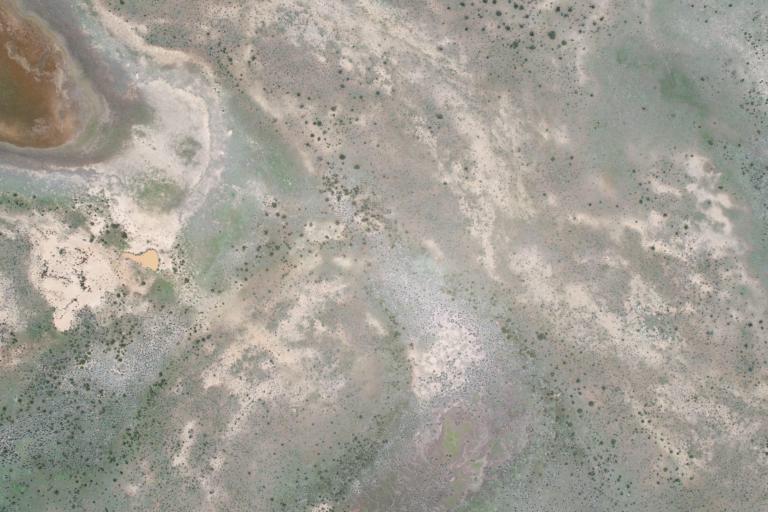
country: BO
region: La Paz
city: Curahuara de Carangas
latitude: -17.2833
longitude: -68.5160
